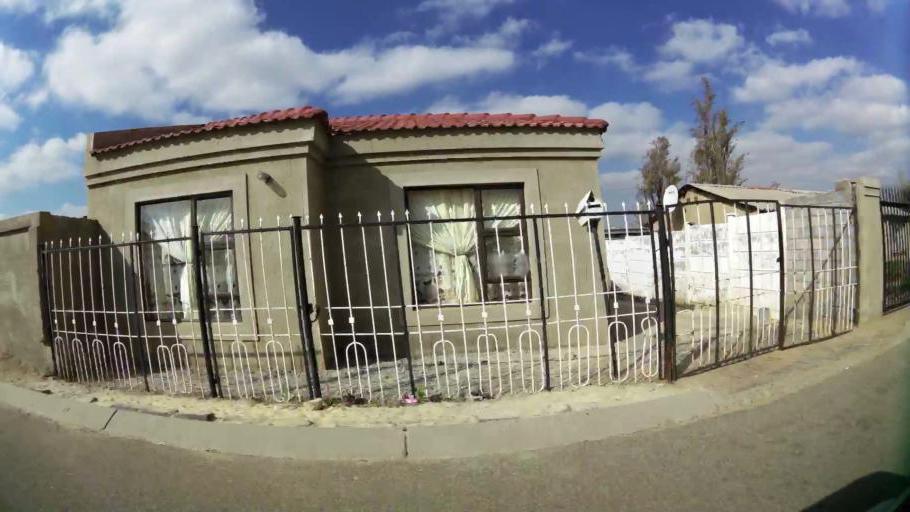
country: ZA
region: Gauteng
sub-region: City of Johannesburg Metropolitan Municipality
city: Roodepoort
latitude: -26.2171
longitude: 27.9038
